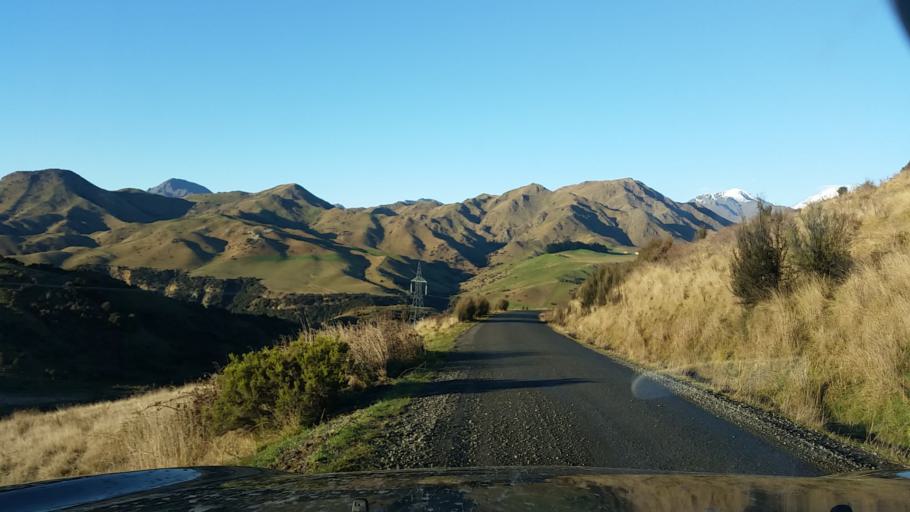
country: NZ
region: Marlborough
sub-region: Marlborough District
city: Blenheim
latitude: -41.7958
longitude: 173.7803
